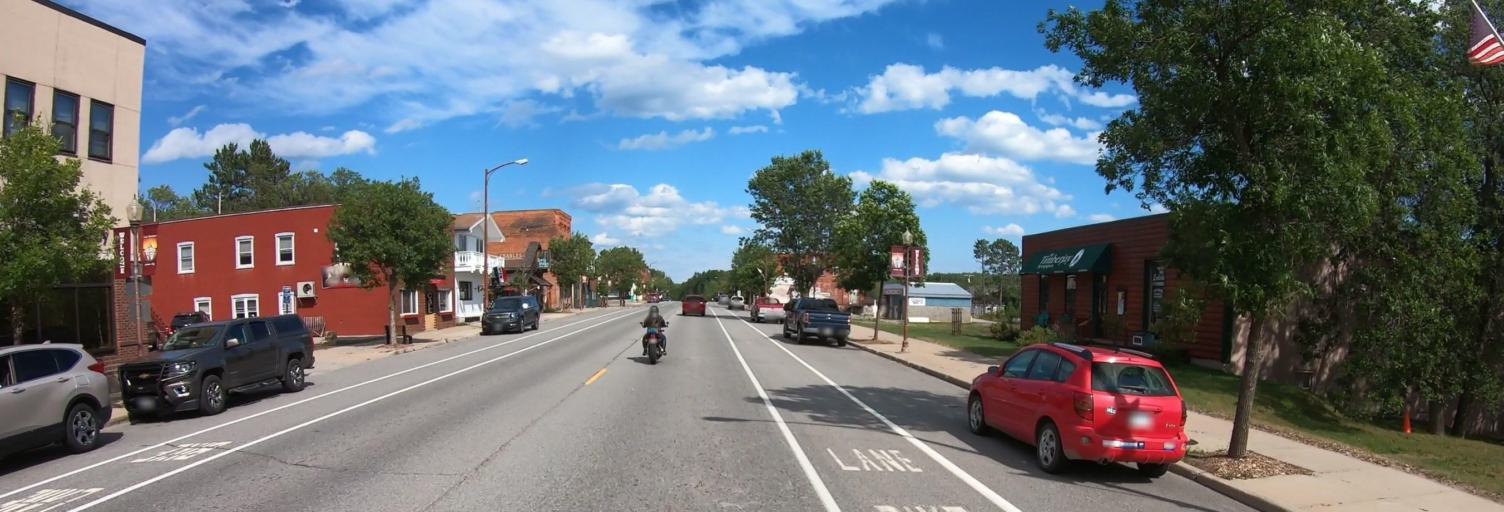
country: US
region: Minnesota
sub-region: Saint Louis County
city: Aurora
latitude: 47.8052
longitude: -92.2748
